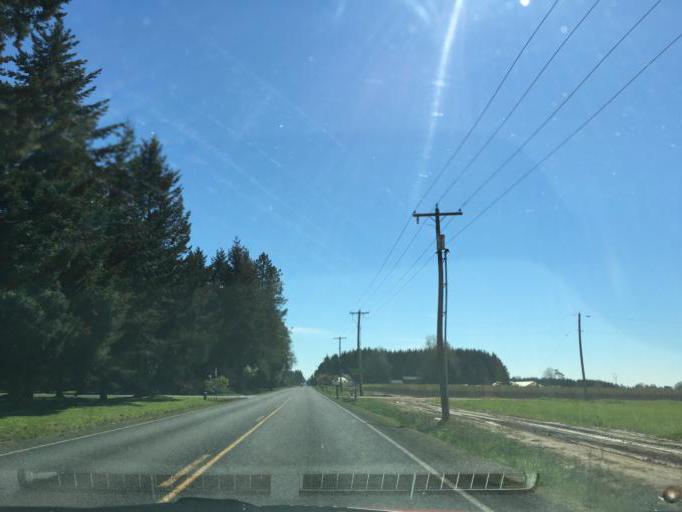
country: US
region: Oregon
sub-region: Clackamas County
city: Canby
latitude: 45.2220
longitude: -122.7228
